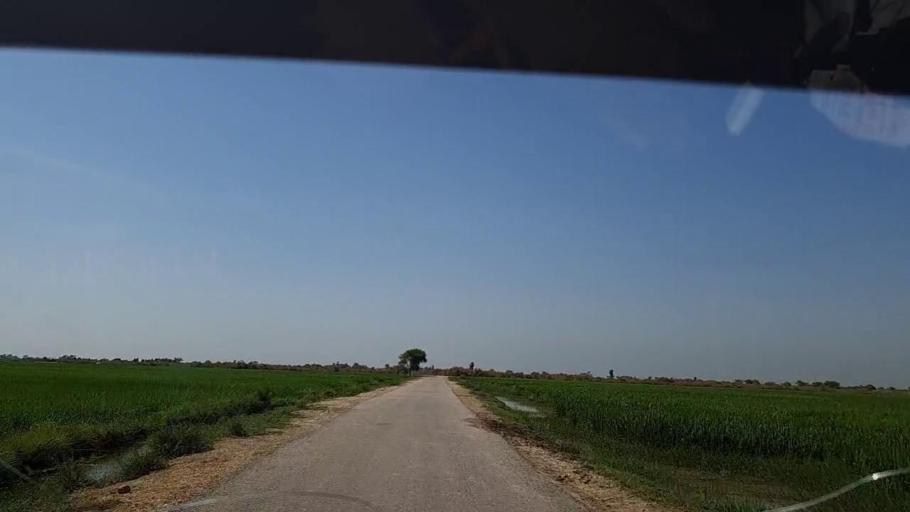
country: PK
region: Sindh
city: Kandhkot
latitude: 28.3117
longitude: 69.1014
